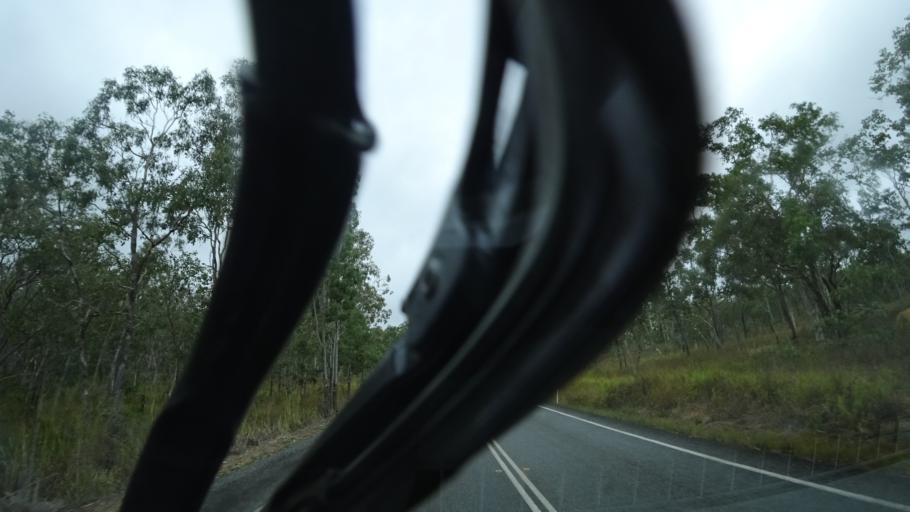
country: AU
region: Queensland
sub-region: Cairns
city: Port Douglas
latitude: -16.6957
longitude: 145.3442
